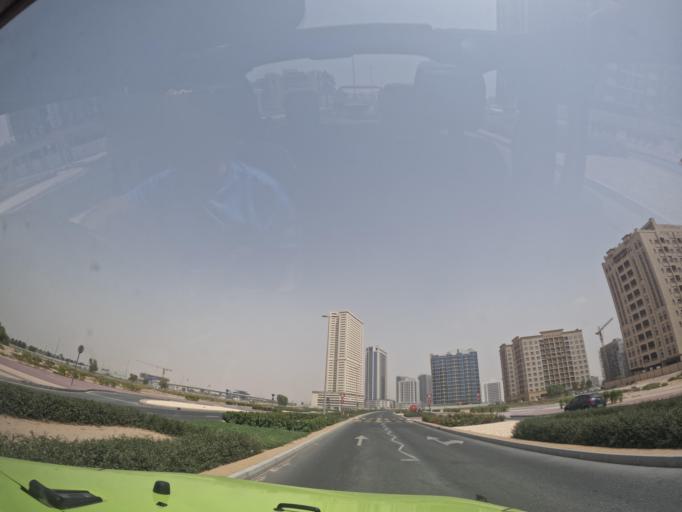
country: AE
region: Dubai
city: Dubai
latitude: 25.0973
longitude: 55.3789
